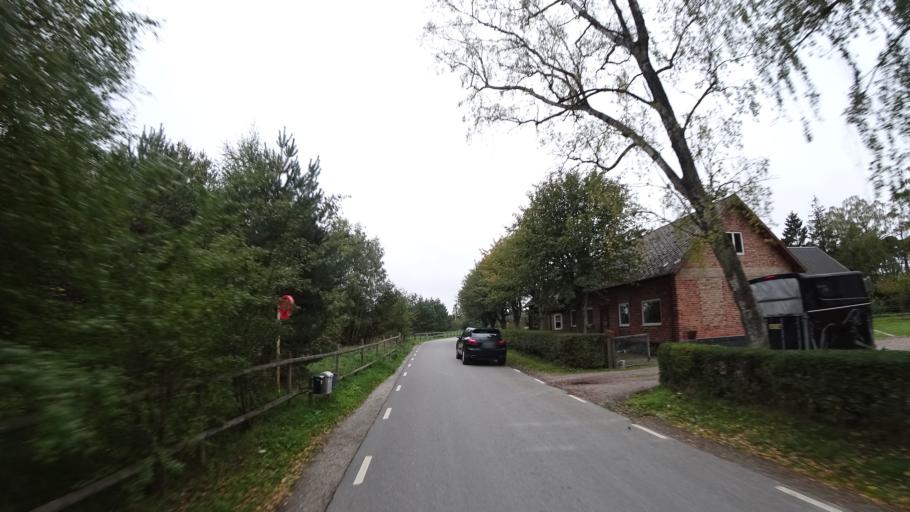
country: SE
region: Skane
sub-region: Kavlinge Kommun
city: Hofterup
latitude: 55.8160
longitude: 12.9956
